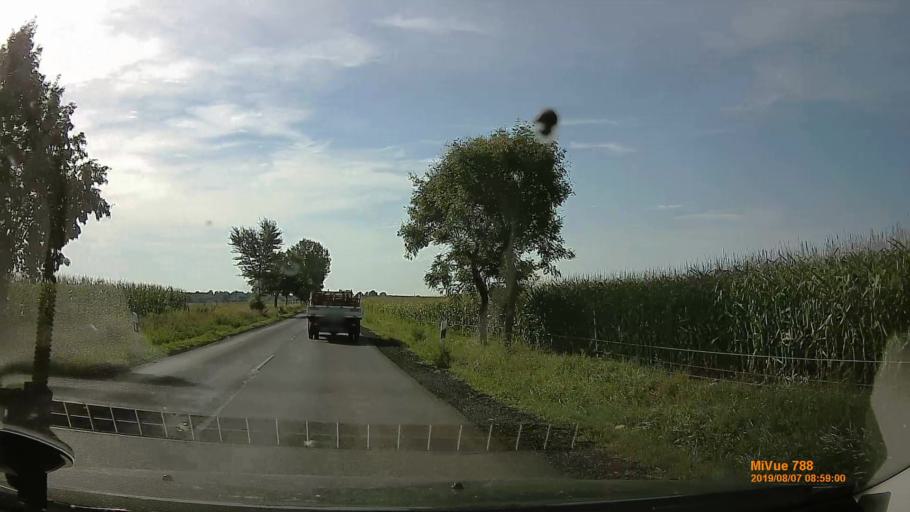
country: HU
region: Zala
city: Pacsa
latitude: 46.7395
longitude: 16.9325
